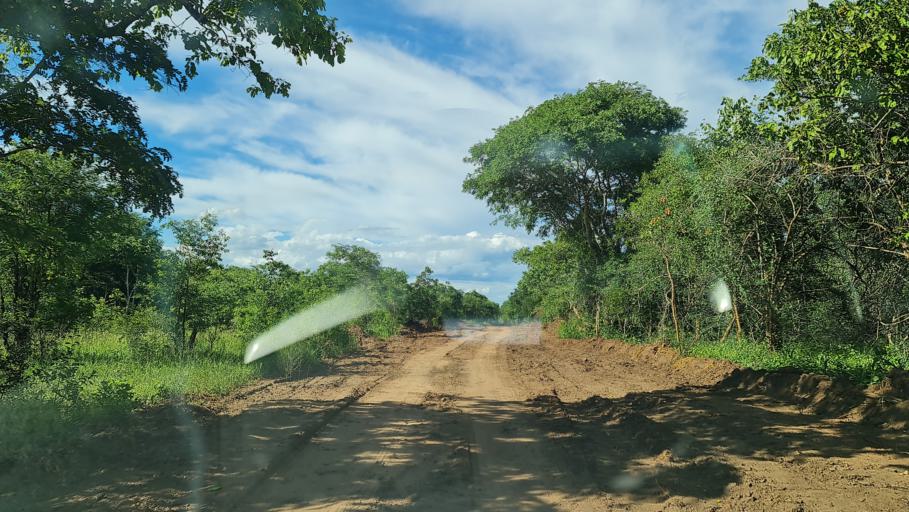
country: MZ
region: Nampula
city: Antonio Enes
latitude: -15.5147
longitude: 40.1306
